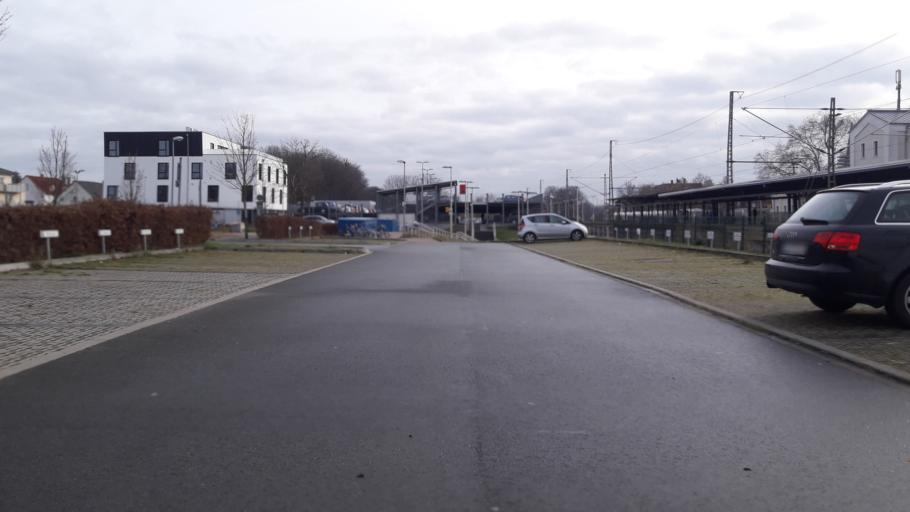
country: DE
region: North Rhine-Westphalia
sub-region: Regierungsbezirk Arnsberg
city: Soest
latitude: 51.5790
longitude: 8.1038
